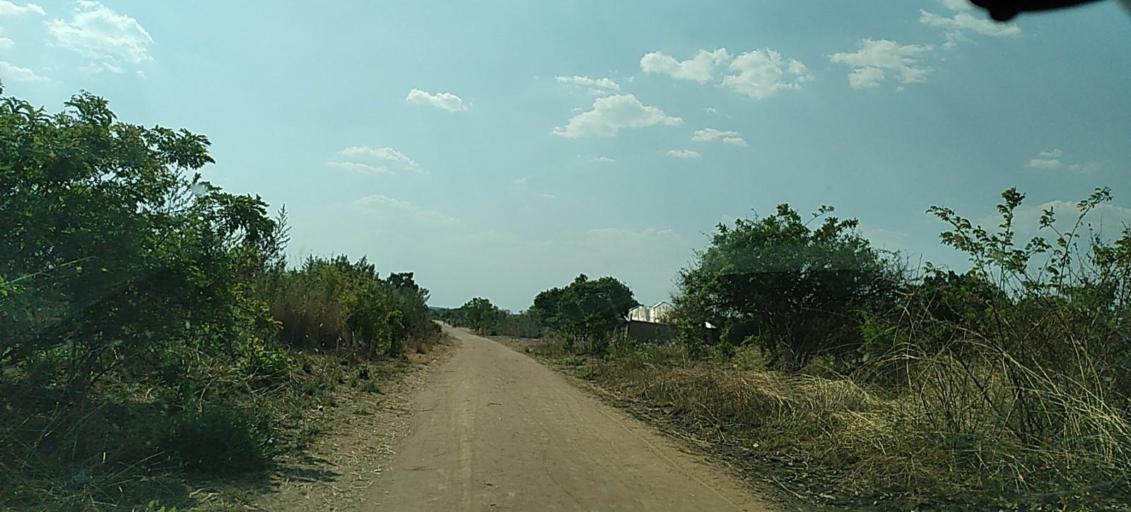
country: ZM
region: North-Western
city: Kalengwa
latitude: -13.1233
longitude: 25.0054
